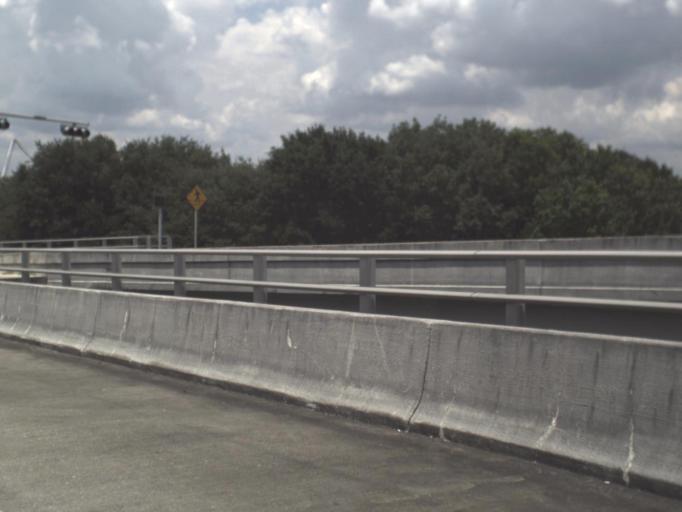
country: US
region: Florida
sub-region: Duval County
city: Jacksonville
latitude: 30.3249
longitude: -81.6684
